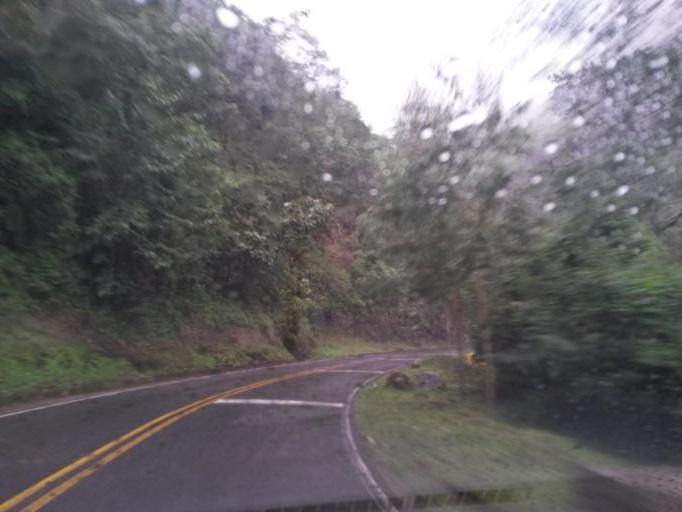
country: CO
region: Cauca
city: Popayan
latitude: 2.3724
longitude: -76.4975
